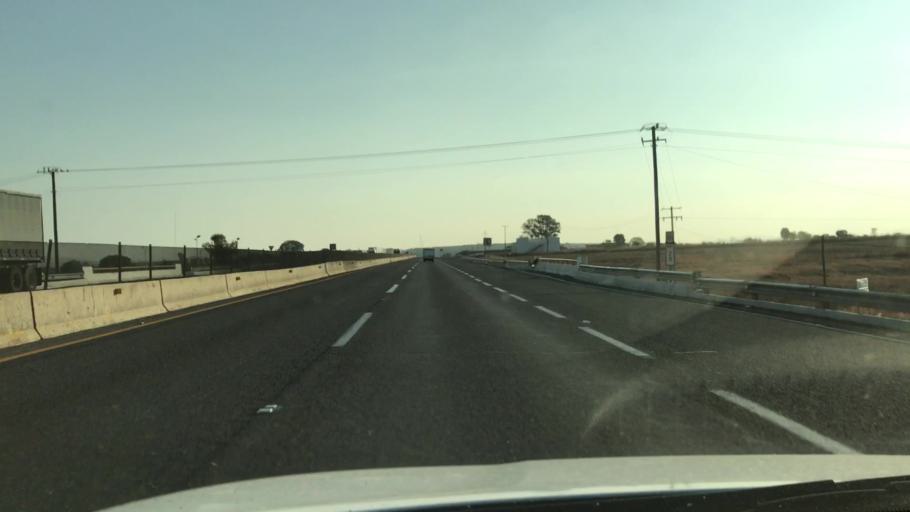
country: MX
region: Jalisco
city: Acatic
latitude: 20.7377
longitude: -102.9109
